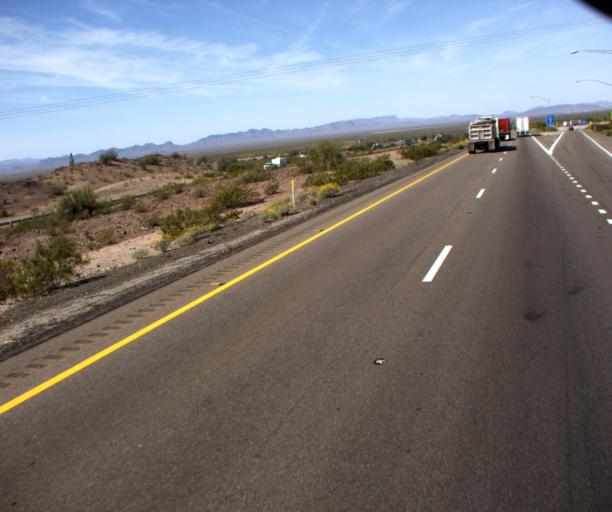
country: US
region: Arizona
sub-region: La Paz County
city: Salome
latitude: 33.6123
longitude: -113.6397
